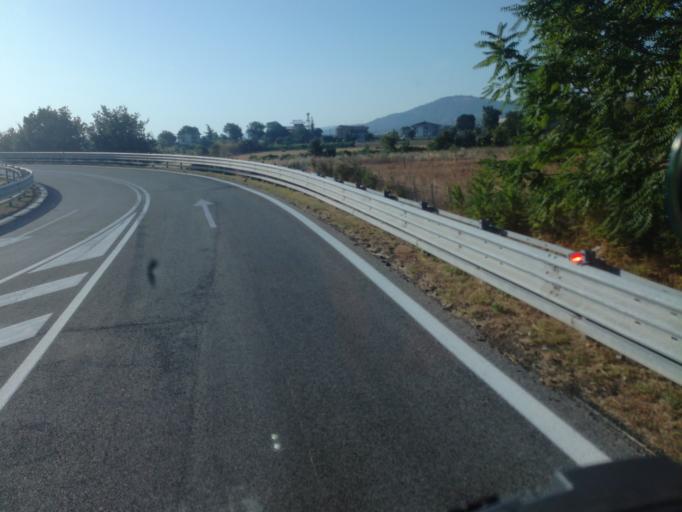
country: IT
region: Campania
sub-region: Provincia di Avellino
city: Grottaminarda
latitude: 41.0633
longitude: 15.0626
